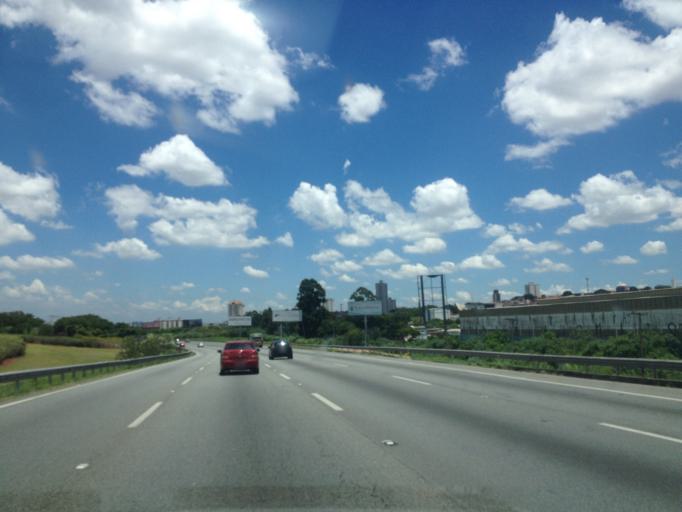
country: BR
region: Sao Paulo
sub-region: Guarulhos
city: Guarulhos
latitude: -23.4945
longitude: -46.5408
